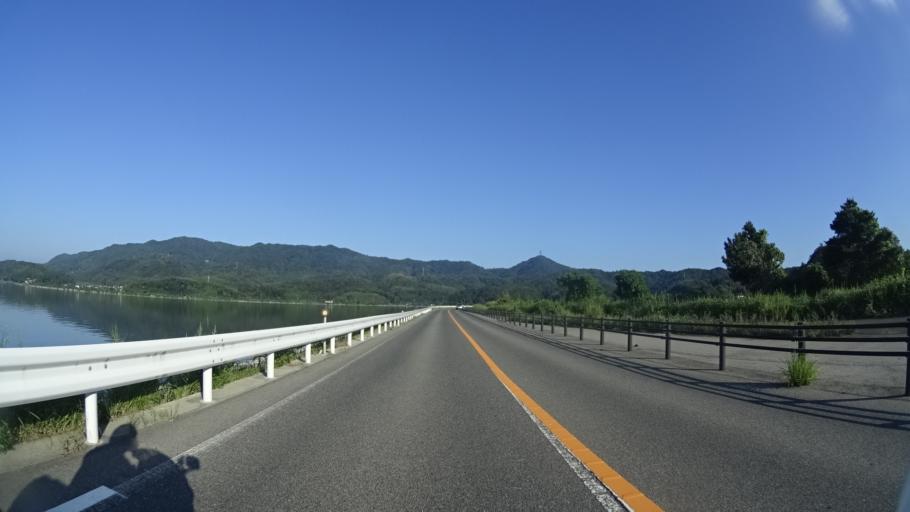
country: JP
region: Shimane
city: Sakaiminato
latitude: 35.5315
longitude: 133.1623
